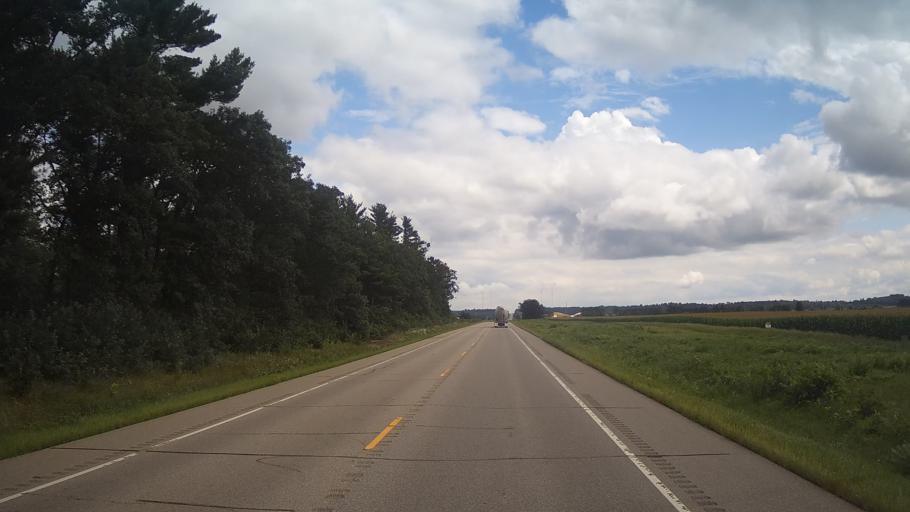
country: US
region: Wisconsin
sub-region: Marquette County
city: Westfield
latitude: 44.0221
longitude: -89.6121
